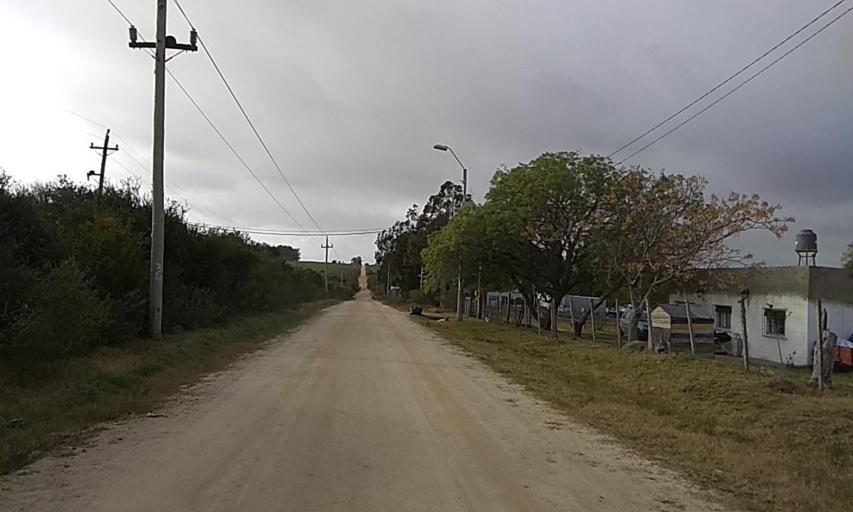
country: UY
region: Florida
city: Florida
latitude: -34.0585
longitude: -56.2186
